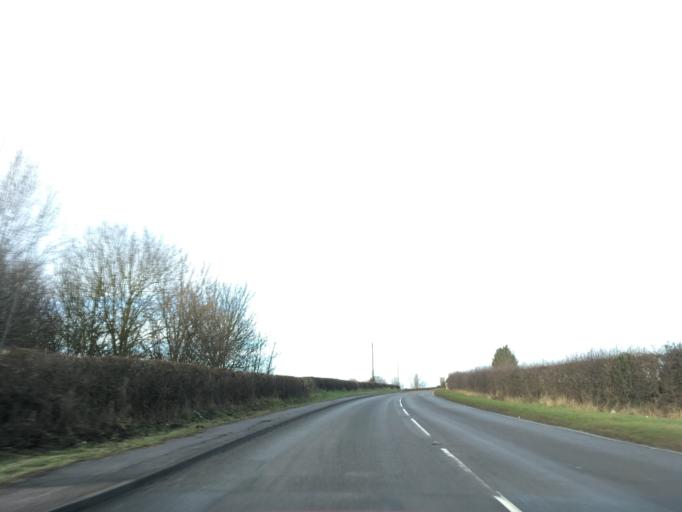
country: GB
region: England
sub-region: Nottinghamshire
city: South Collingham
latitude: 53.1594
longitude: -0.7613
